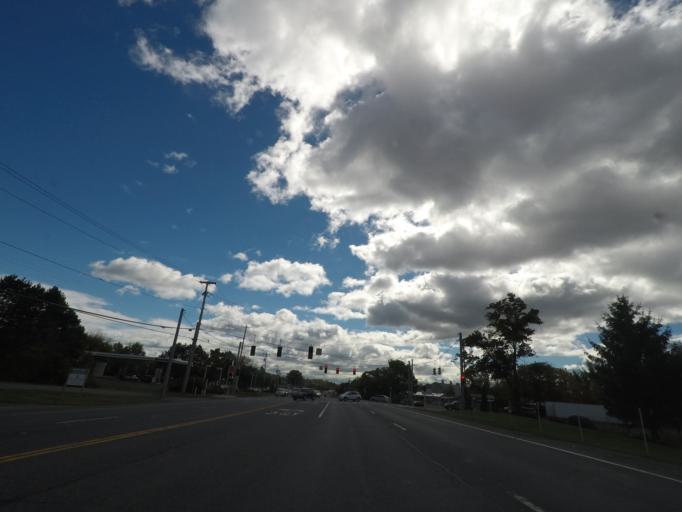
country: US
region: New York
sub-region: Saratoga County
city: Country Knolls
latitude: 42.8506
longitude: -73.7554
